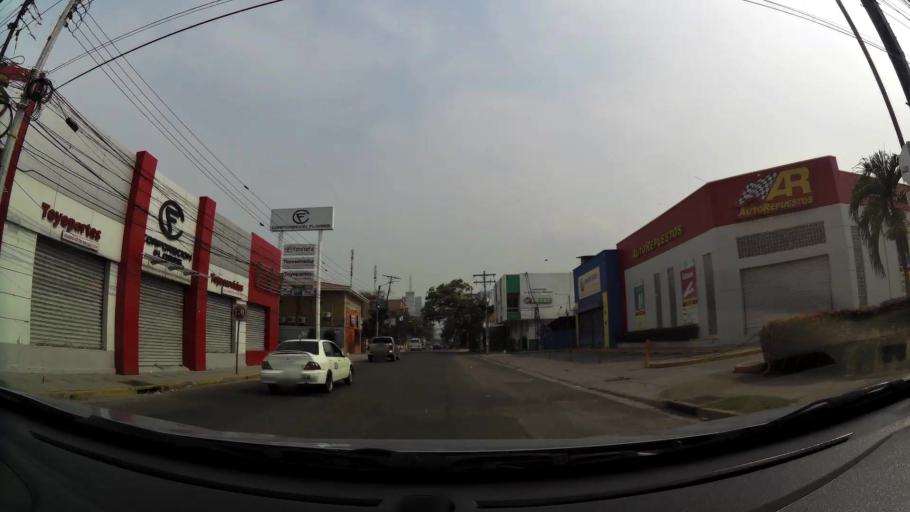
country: HN
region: Cortes
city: San Pedro Sula
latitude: 15.5100
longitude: -88.0240
